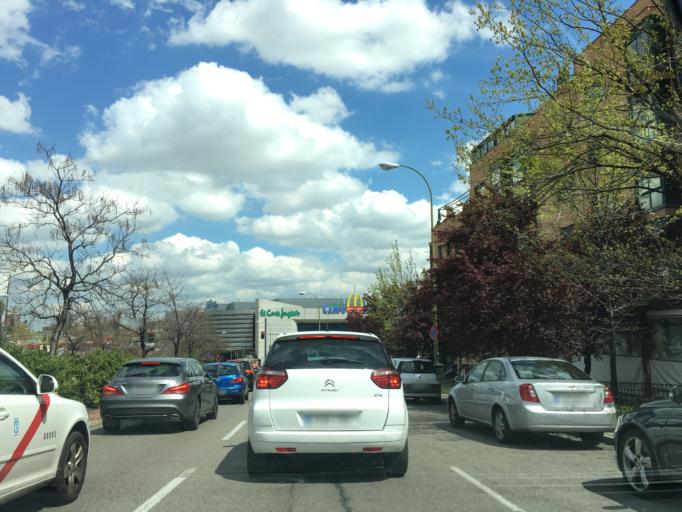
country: ES
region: Madrid
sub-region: Provincia de Madrid
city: San Blas
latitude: 40.4553
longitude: -3.6201
